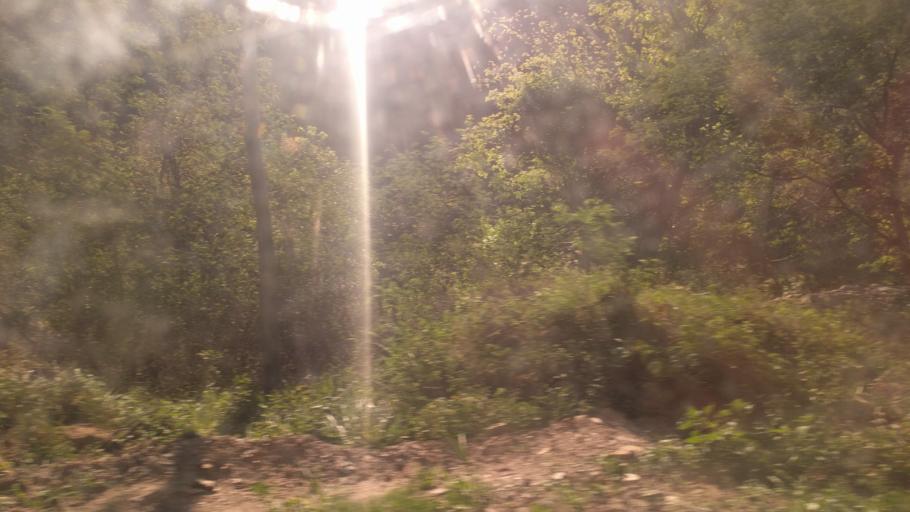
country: BO
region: Santa Cruz
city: Jorochito
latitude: -18.1701
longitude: -63.5806
